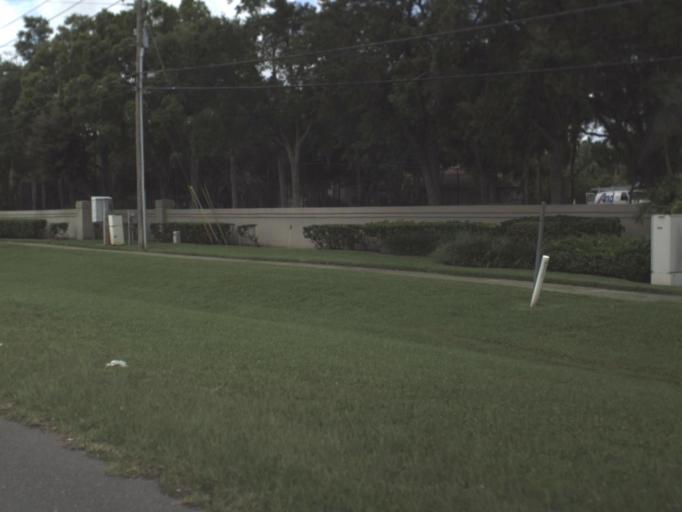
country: US
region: Florida
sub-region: Pinellas County
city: Saint George
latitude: 28.0530
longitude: -82.7107
